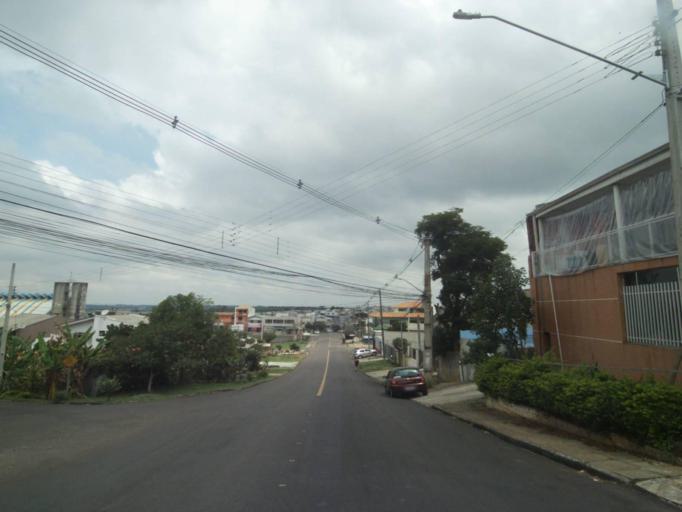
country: BR
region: Parana
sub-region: Curitiba
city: Curitiba
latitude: -25.4957
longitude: -49.3518
